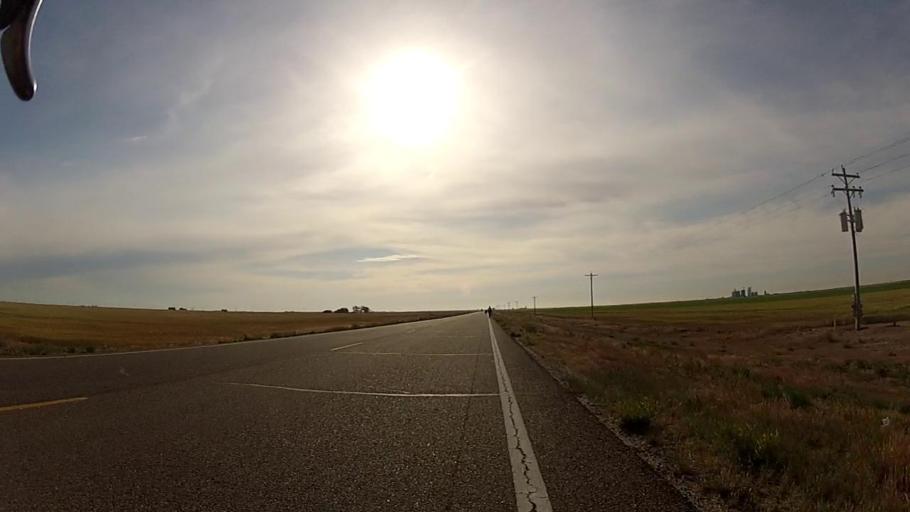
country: US
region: Kansas
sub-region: Grant County
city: Ulysses
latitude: 37.5766
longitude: -101.4810
